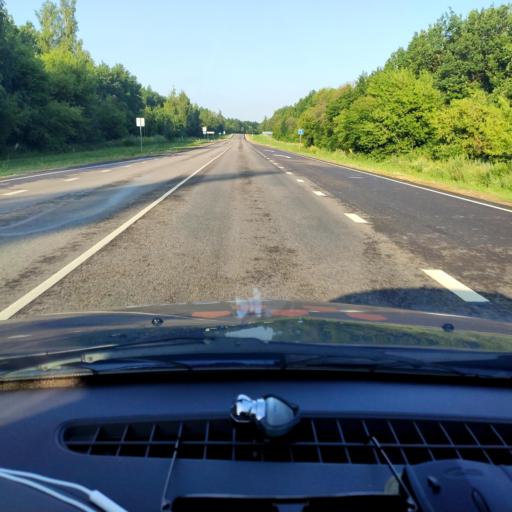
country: RU
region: Lipetsk
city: Izmalkovo
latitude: 52.4535
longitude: 38.0023
